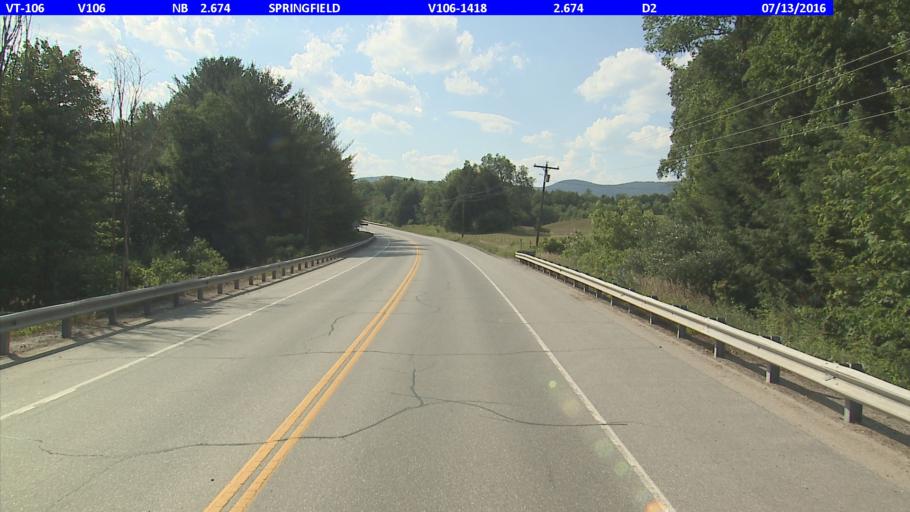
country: US
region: Vermont
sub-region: Windsor County
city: Springfield
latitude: 43.3359
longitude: -72.5196
